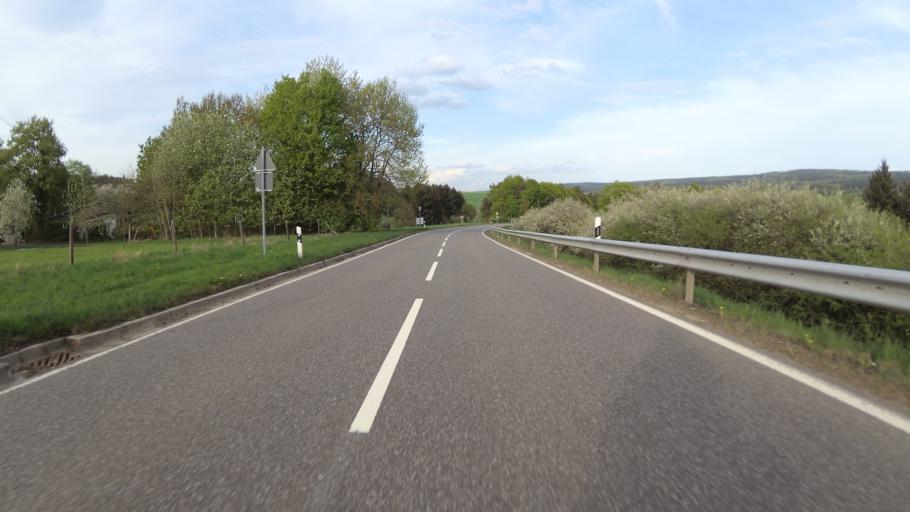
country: DE
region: Rheinland-Pfalz
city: Morbach
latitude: 49.8192
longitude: 7.1304
